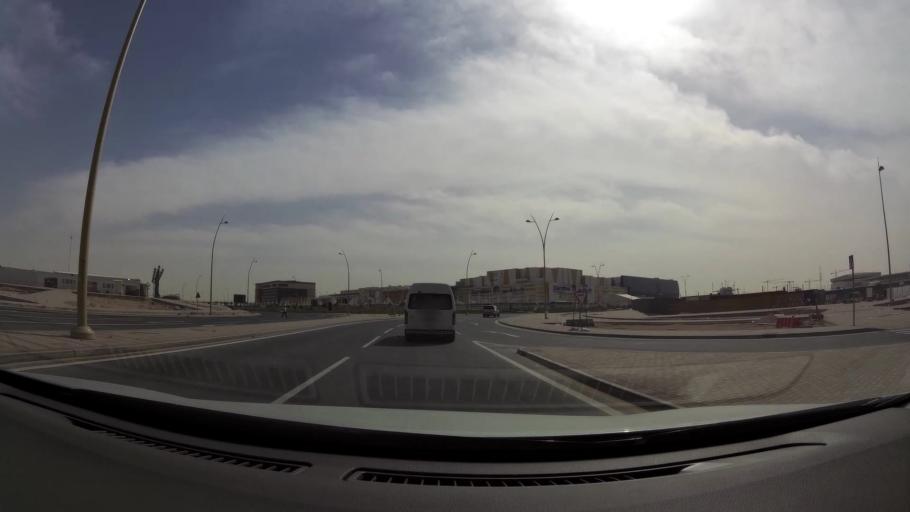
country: QA
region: Baladiyat ar Rayyan
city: Ar Rayyan
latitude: 25.3304
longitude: 51.3528
